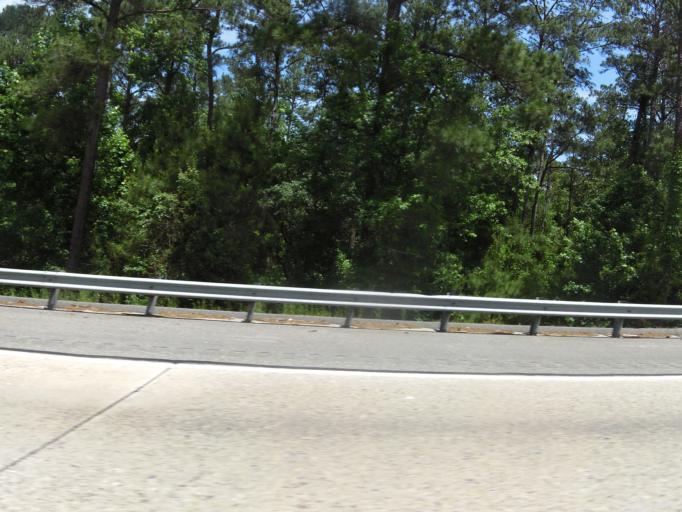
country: US
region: Georgia
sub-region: Chatham County
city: Bloomingdale
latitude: 32.1436
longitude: -81.4155
